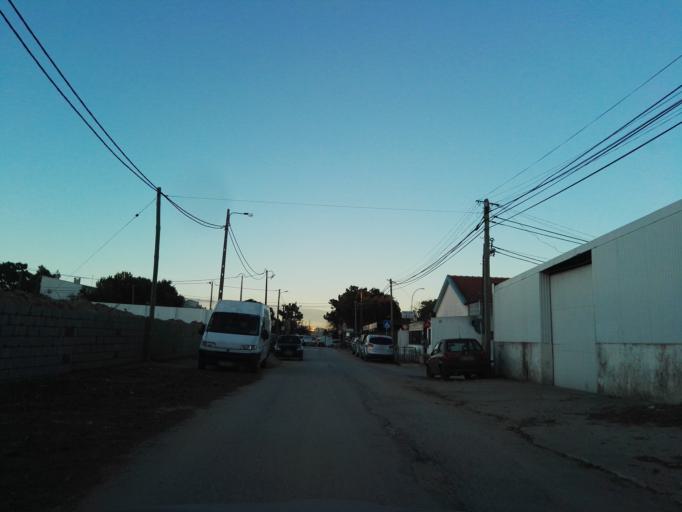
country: PT
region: Setubal
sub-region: Seixal
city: Corroios
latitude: 38.6278
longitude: -9.1456
